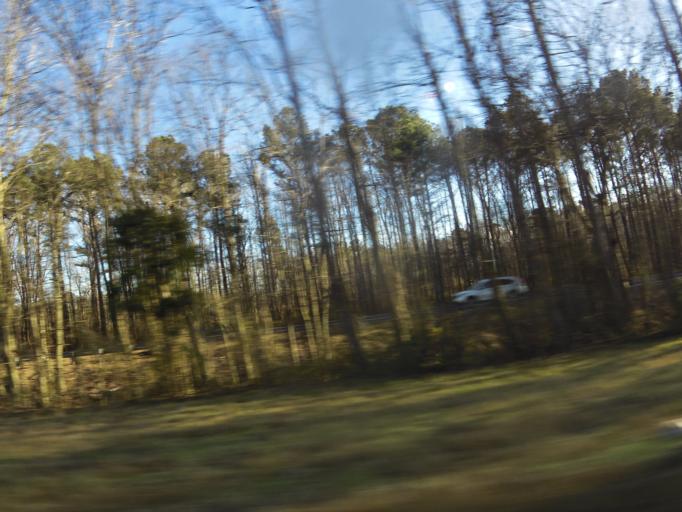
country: US
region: Virginia
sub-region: City of Portsmouth
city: Portsmouth Heights
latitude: 36.7777
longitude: -76.4415
